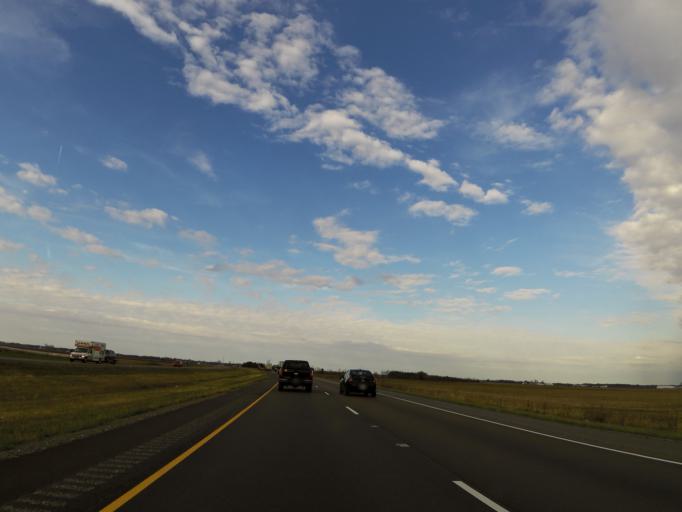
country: US
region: Illinois
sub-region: Washington County
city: Okawville
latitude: 38.4302
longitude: -89.4934
